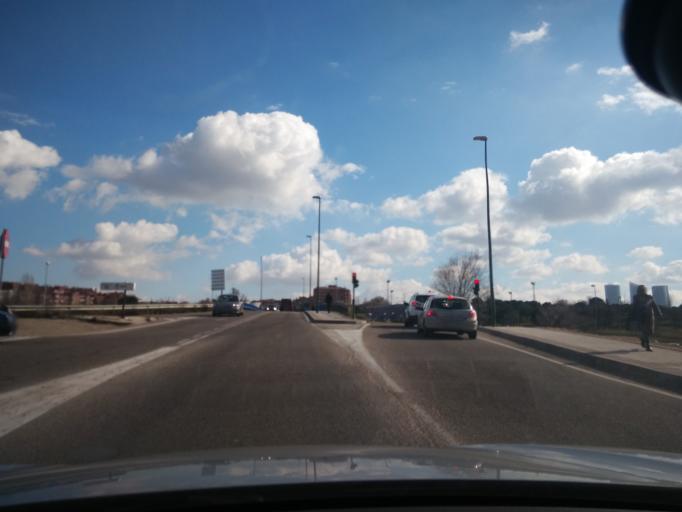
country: ES
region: Madrid
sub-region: Provincia de Madrid
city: Las Tablas
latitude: 40.5022
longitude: -3.6972
